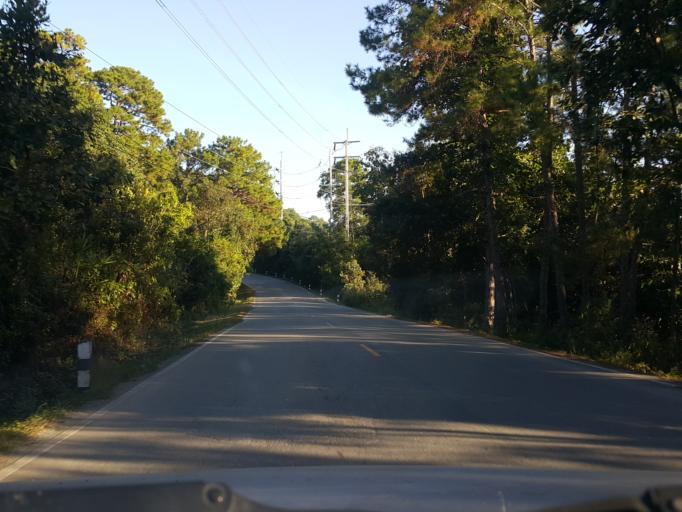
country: TH
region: Mae Hong Son
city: Mae Hi
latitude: 19.2718
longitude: 98.5643
